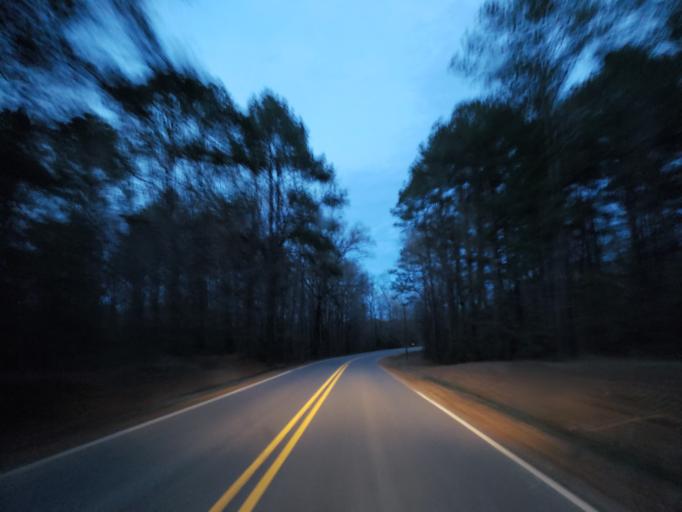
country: US
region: Alabama
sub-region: Greene County
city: Eutaw
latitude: 32.9017
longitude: -88.0273
